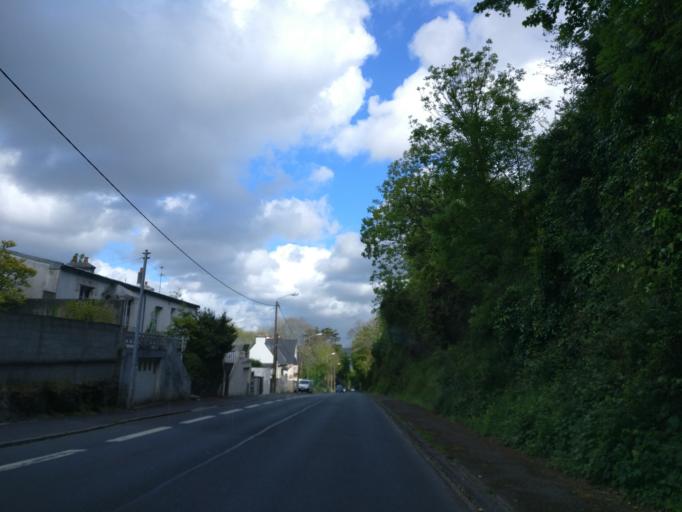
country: FR
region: Brittany
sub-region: Departement du Finistere
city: Brest
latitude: 48.3993
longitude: -4.4434
